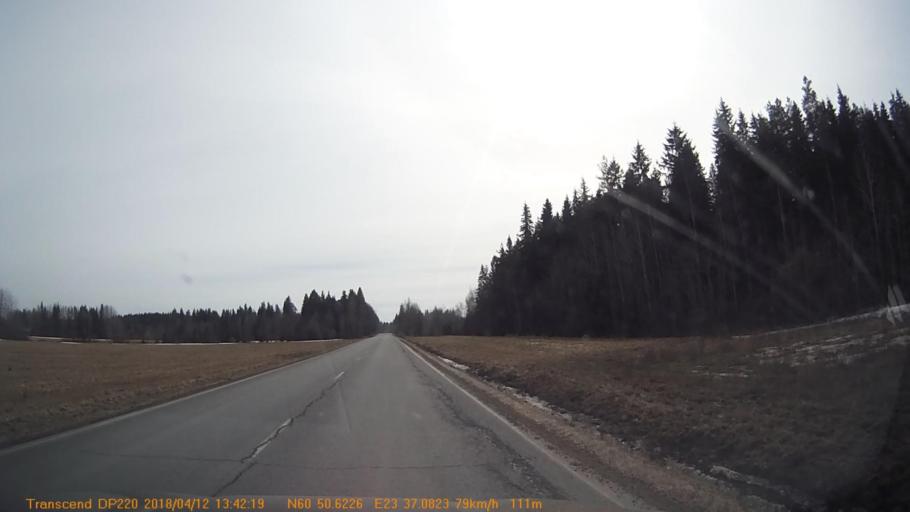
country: FI
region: Haeme
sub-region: Forssa
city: Forssa
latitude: 60.8430
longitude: 23.6181
